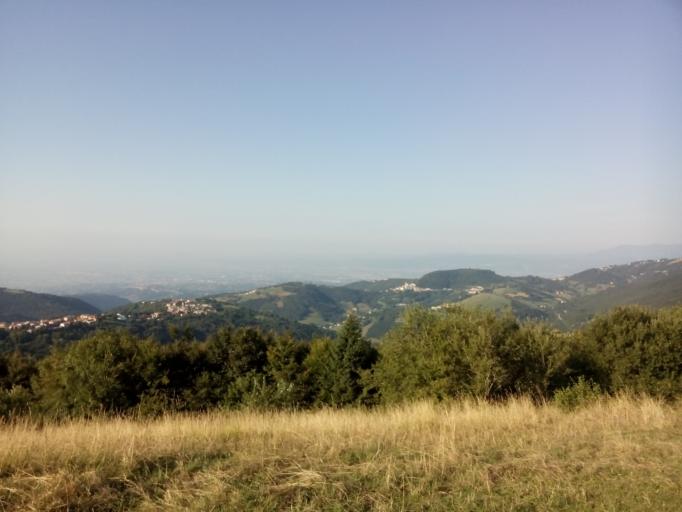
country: IT
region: Veneto
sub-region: Provincia di Vicenza
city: Conco
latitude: 45.8161
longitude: 11.6138
